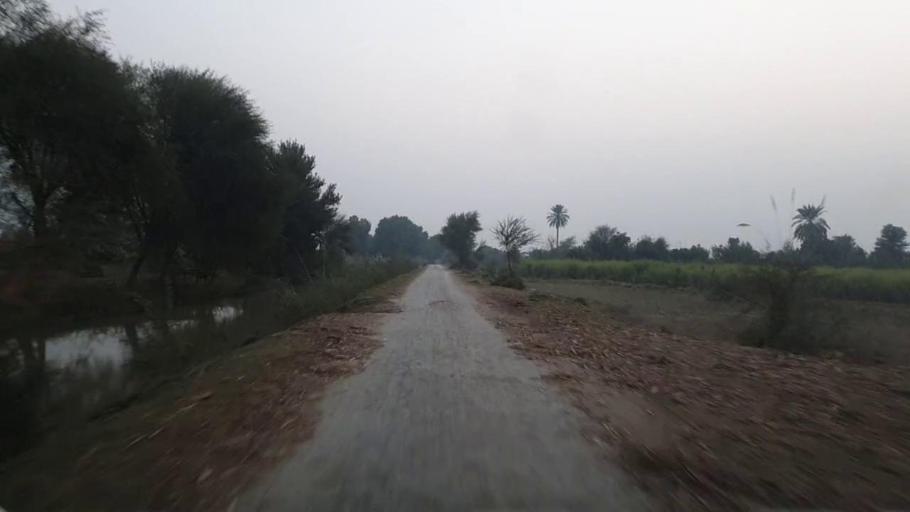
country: PK
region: Sindh
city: Karaundi
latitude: 26.9326
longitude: 68.4406
